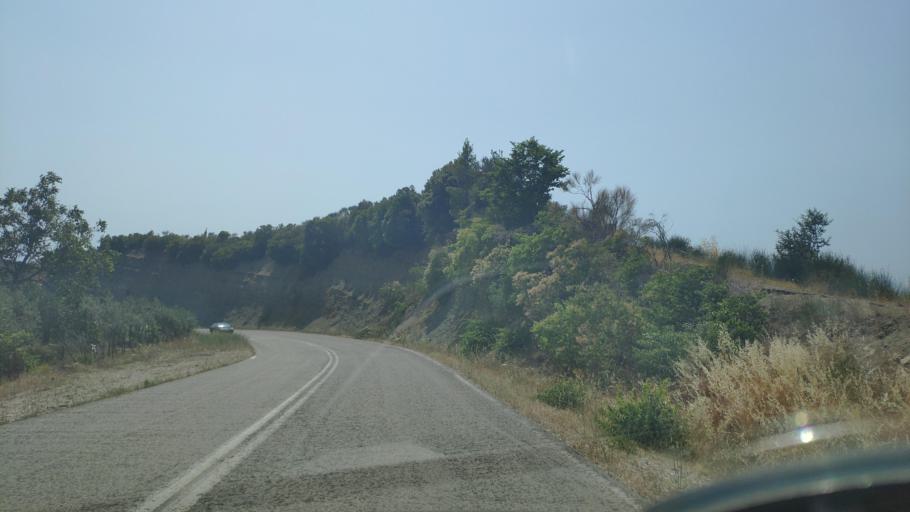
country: GR
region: Epirus
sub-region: Nomos Artas
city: Peta
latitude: 39.1861
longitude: 21.0973
